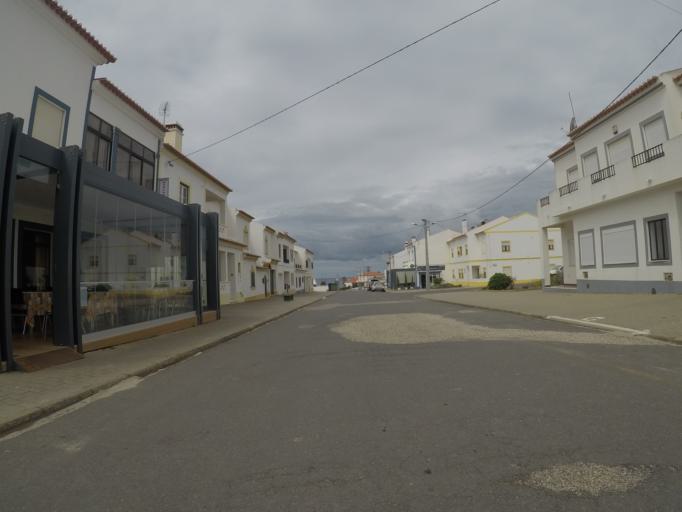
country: PT
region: Beja
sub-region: Odemira
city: Sao Teotonio
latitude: 37.5254
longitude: -8.7848
